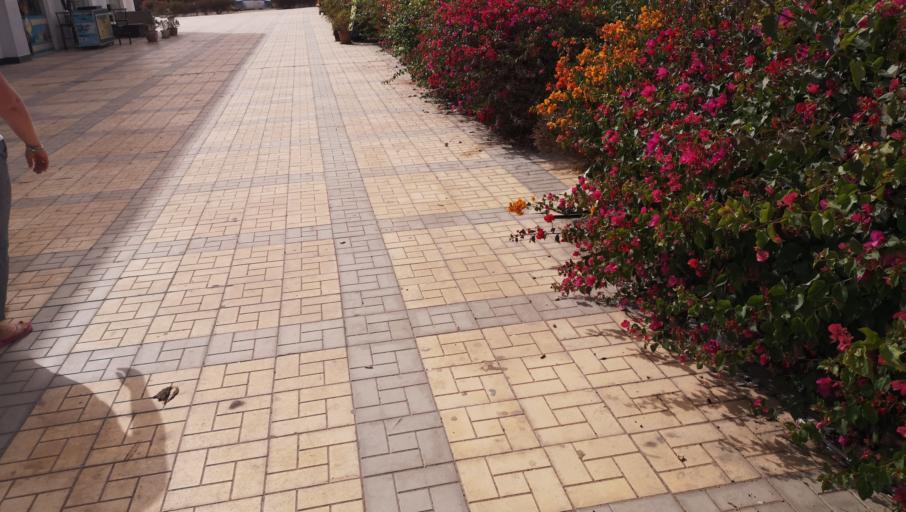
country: EG
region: South Sinai
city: Sharm el-Sheikh
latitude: 27.8660
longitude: 34.3141
